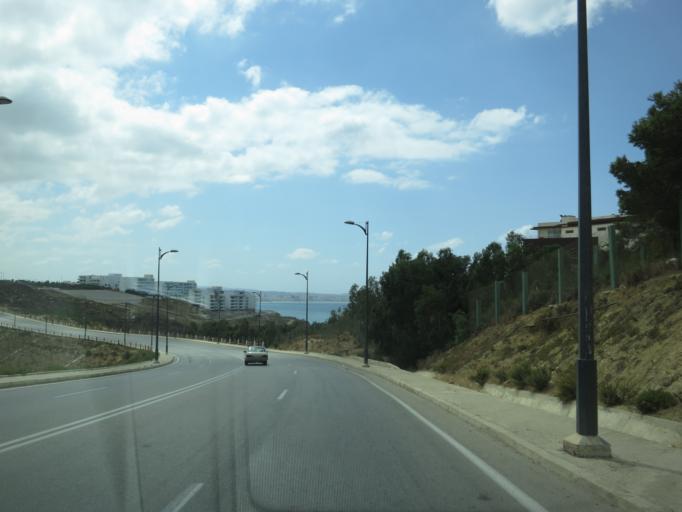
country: MA
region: Tanger-Tetouan
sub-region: Tanger-Assilah
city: Tangier
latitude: 35.8078
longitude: -5.7414
